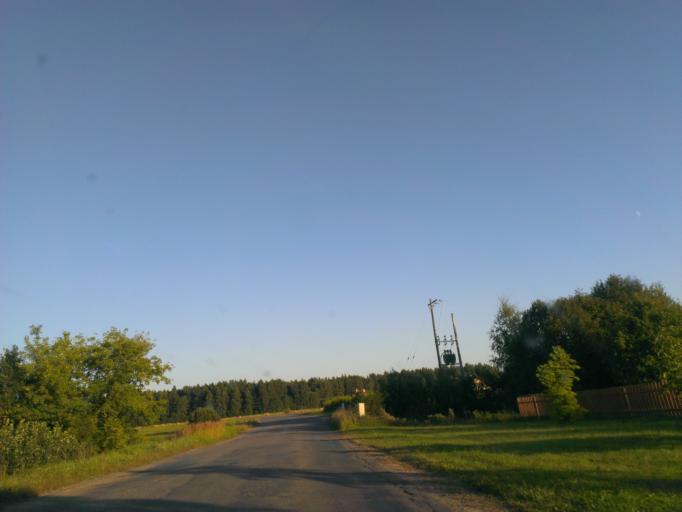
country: LV
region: Garkalne
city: Garkalne
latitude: 57.0644
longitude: 24.3779
